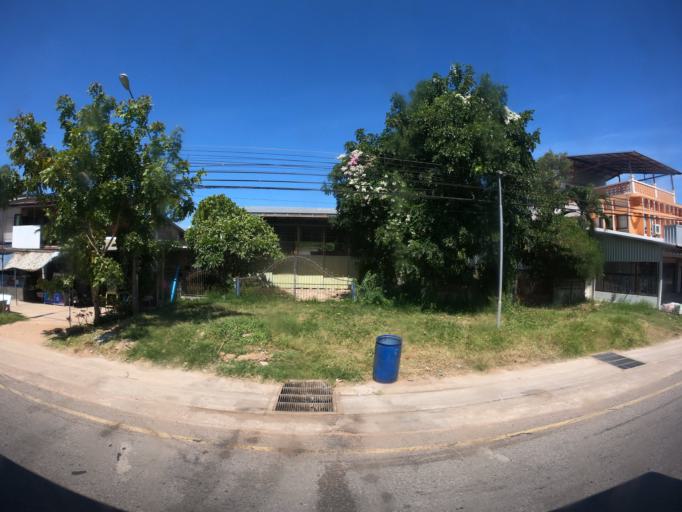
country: TH
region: Khon Kaen
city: Ban Phai
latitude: 16.0574
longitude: 102.7184
